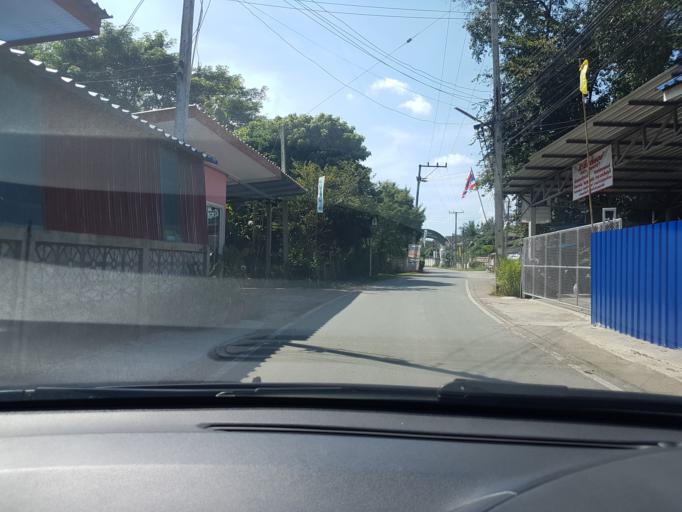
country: TH
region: Lampang
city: Ko Kha
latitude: 18.2154
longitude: 99.4102
